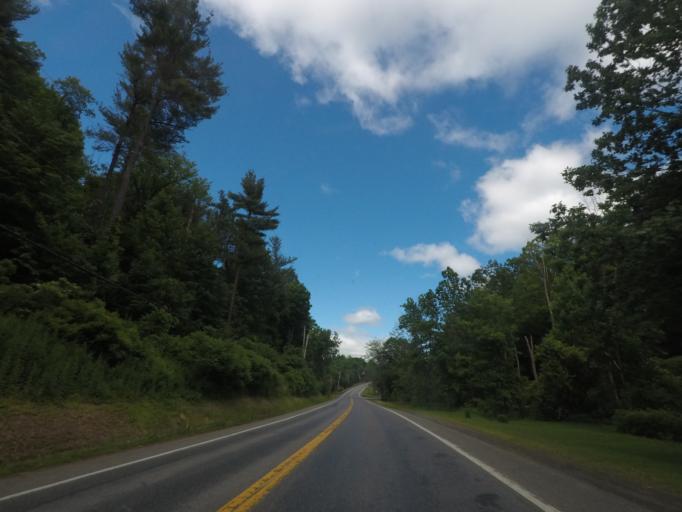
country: US
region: New York
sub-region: Columbia County
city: Philmont
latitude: 42.2070
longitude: -73.6679
